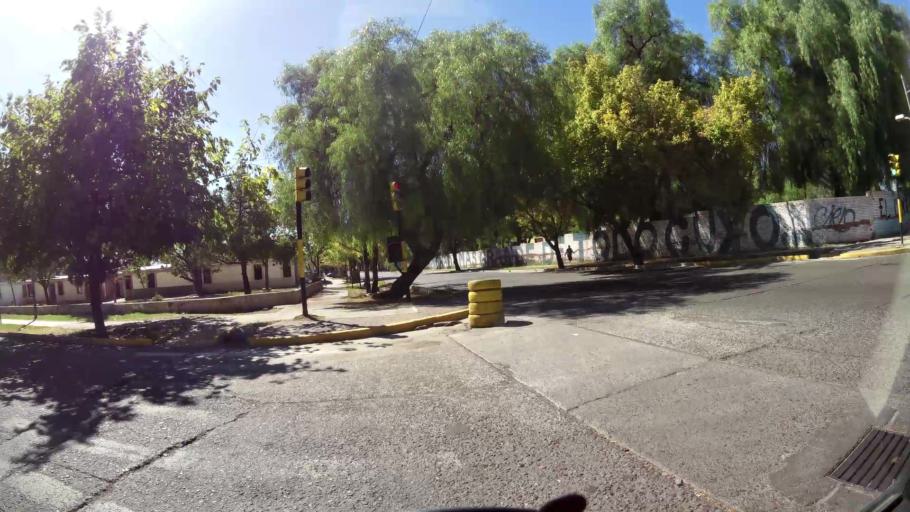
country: AR
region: Mendoza
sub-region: Departamento de Godoy Cruz
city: Godoy Cruz
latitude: -32.9075
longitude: -68.8706
